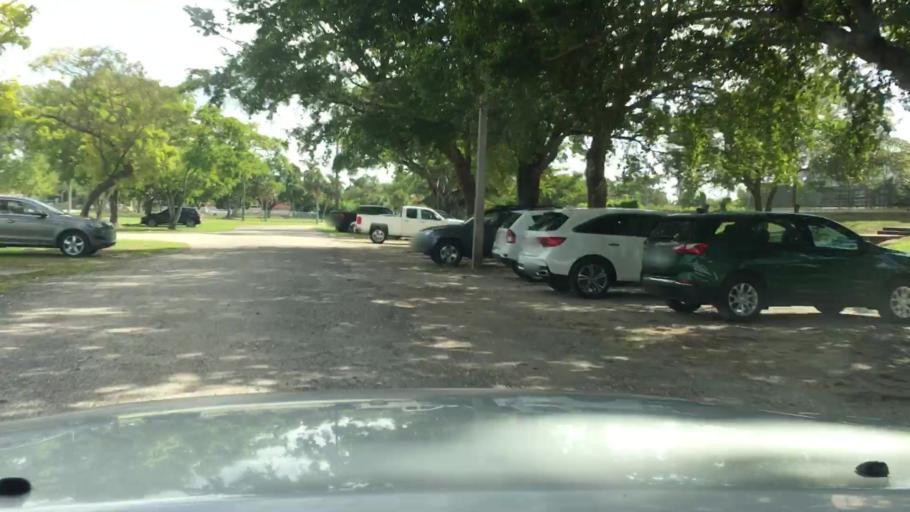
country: US
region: Florida
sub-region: Miami-Dade County
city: University Park
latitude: 25.7487
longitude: -80.3765
